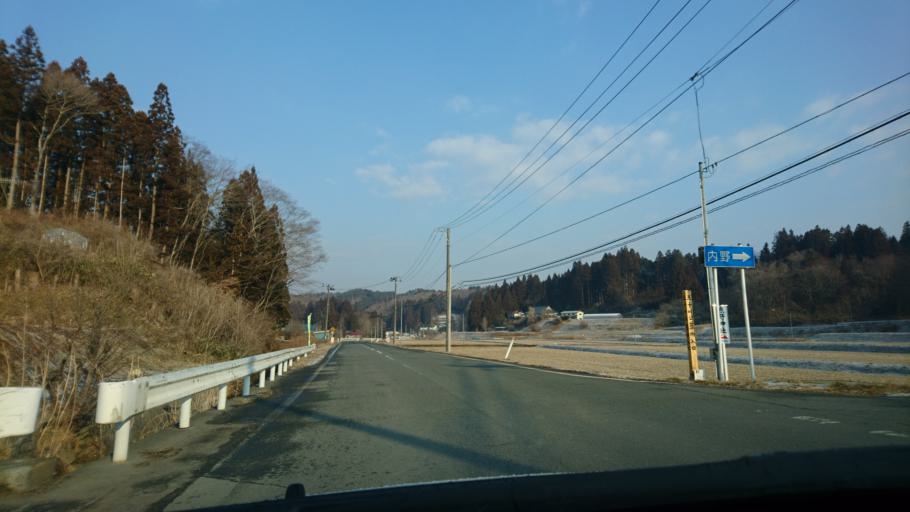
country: JP
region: Iwate
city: Ichinoseki
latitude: 38.9280
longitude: 141.3859
